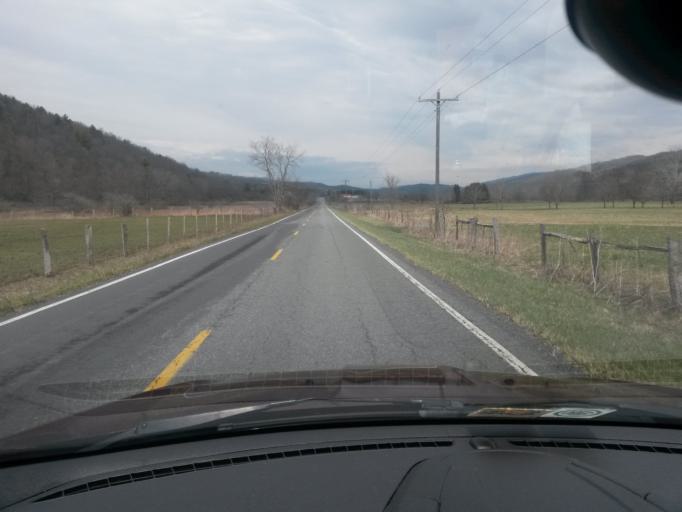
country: US
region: Virginia
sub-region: Highland County
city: Monterey
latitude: 38.2543
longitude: -79.6772
